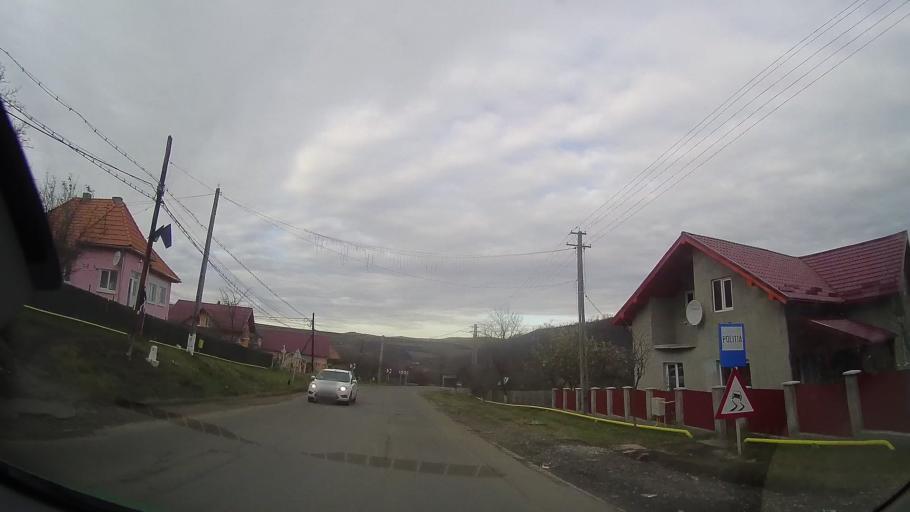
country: RO
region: Bistrita-Nasaud
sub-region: Comuna Silvasu de Campie
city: Silvasu de Campie
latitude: 46.7802
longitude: 24.2925
